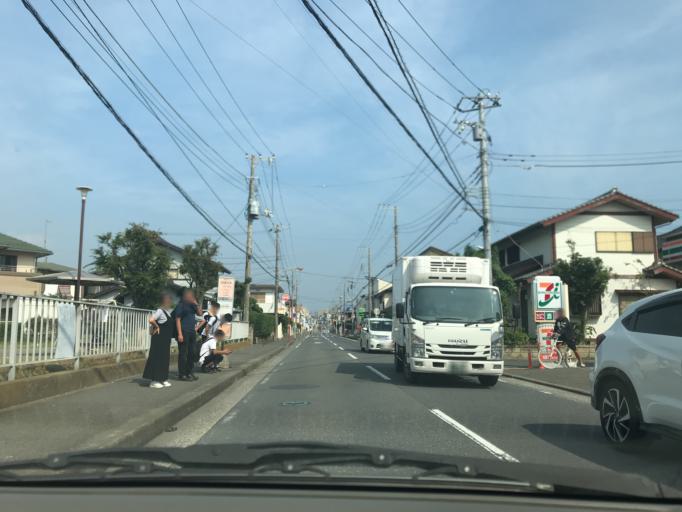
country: JP
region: Kanagawa
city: Chigasaki
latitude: 35.3226
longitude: 139.3887
